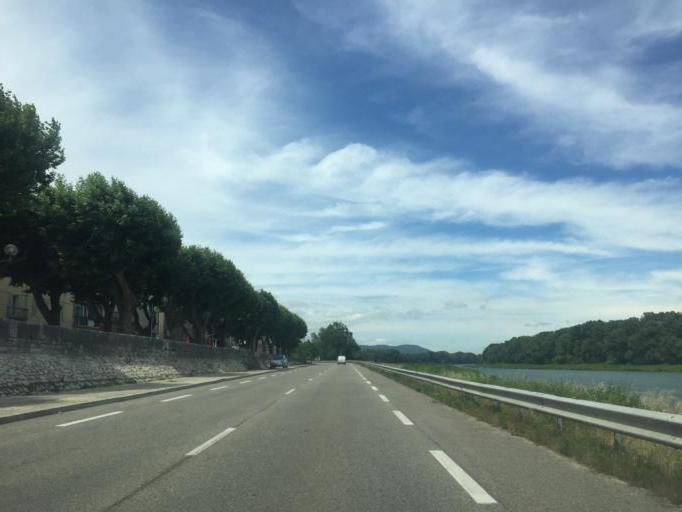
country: FR
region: Rhone-Alpes
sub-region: Departement de l'Ardeche
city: Bourg-Saint-Andeol
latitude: 44.3697
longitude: 4.6477
